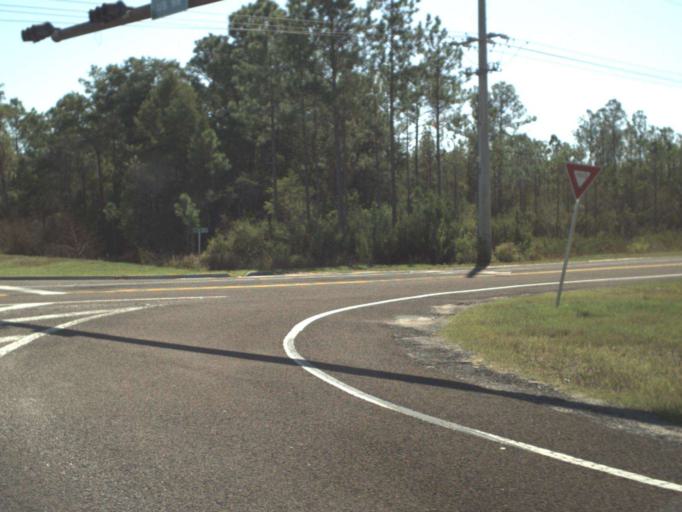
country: US
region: Florida
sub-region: Walton County
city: Seaside
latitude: 30.3593
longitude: -86.1562
